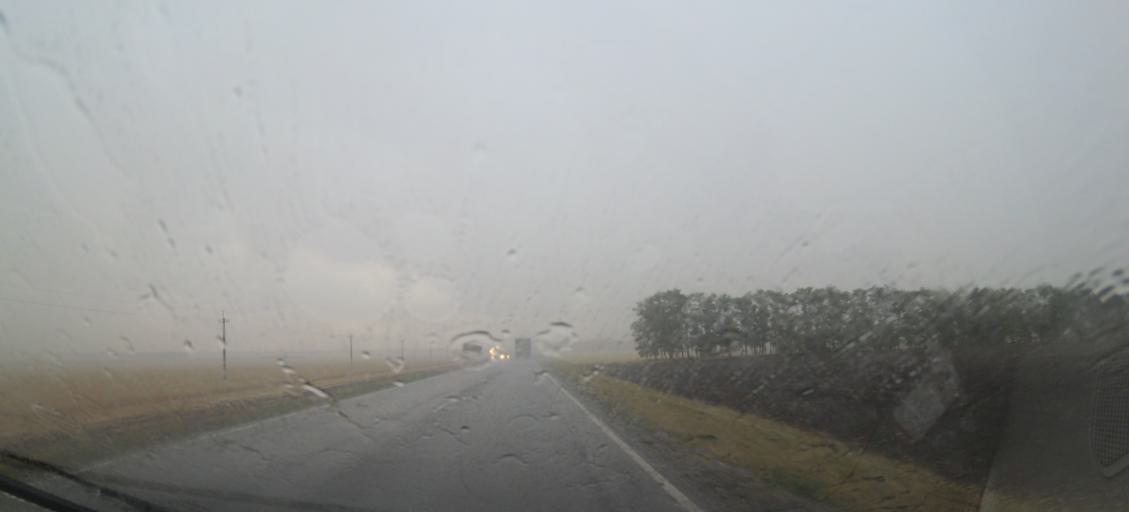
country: RU
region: Rostov
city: Gundorovskiy
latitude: 46.8497
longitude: 41.9133
